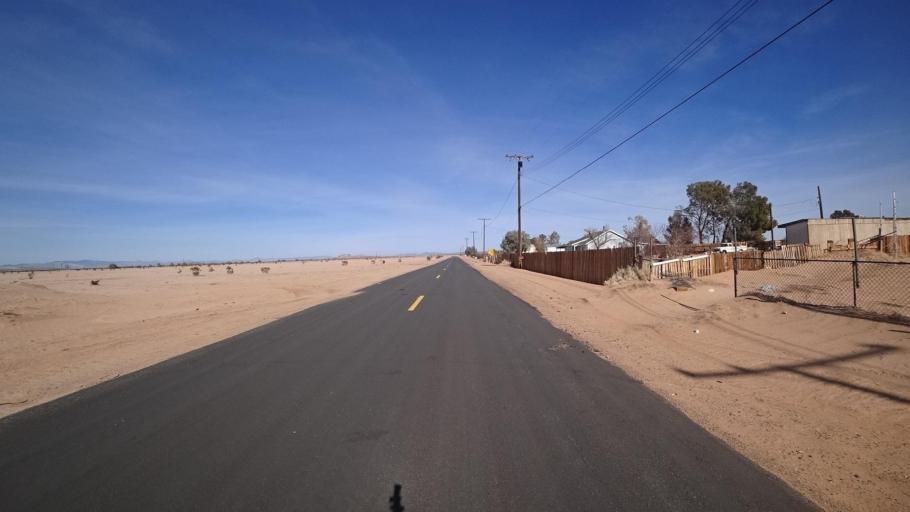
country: US
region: California
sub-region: Kern County
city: North Edwards
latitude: 35.0928
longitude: -117.7927
